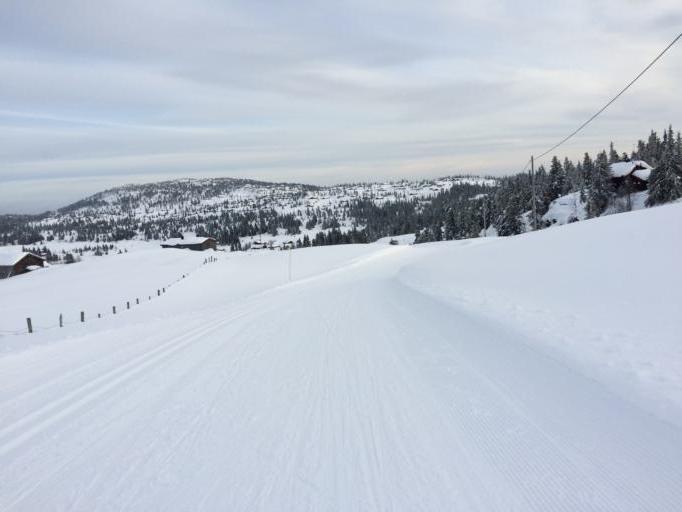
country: NO
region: Oppland
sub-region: Gausdal
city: Segalstad bru
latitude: 61.3147
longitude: 10.0520
